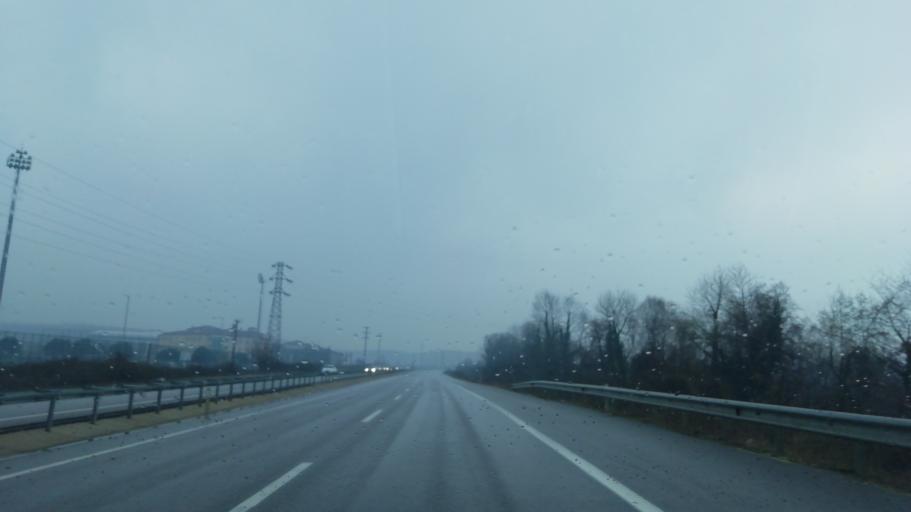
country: TR
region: Sakarya
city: Akyazi
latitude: 40.6685
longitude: 30.5902
